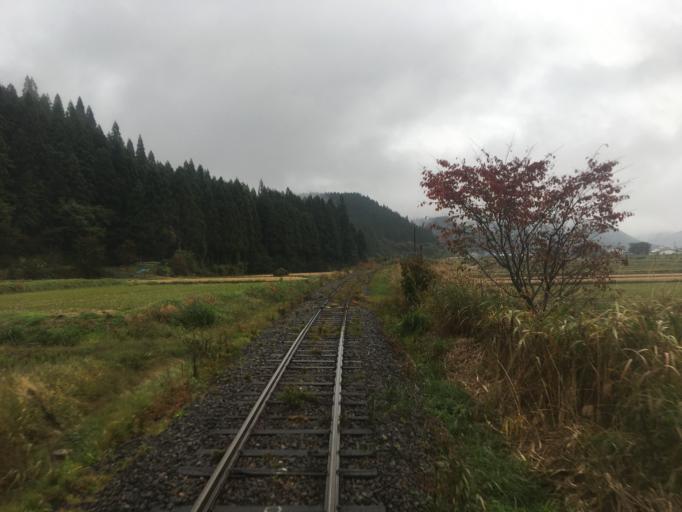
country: JP
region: Yamagata
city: Obanazawa
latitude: 38.7481
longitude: 140.5337
